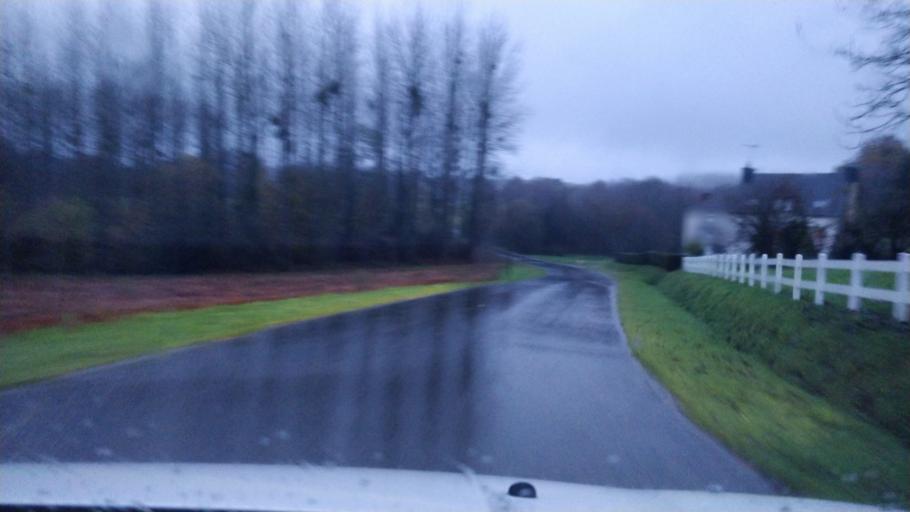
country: FR
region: Brittany
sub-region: Departement du Morbihan
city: Meneac
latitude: 48.1974
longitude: -2.5098
